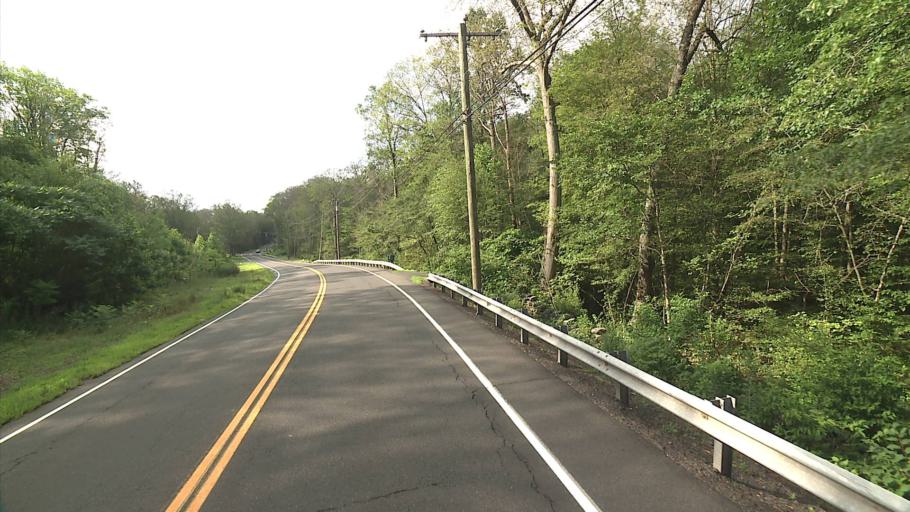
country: US
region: Connecticut
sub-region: Middlesex County
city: Higganum
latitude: 41.4135
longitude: -72.5634
